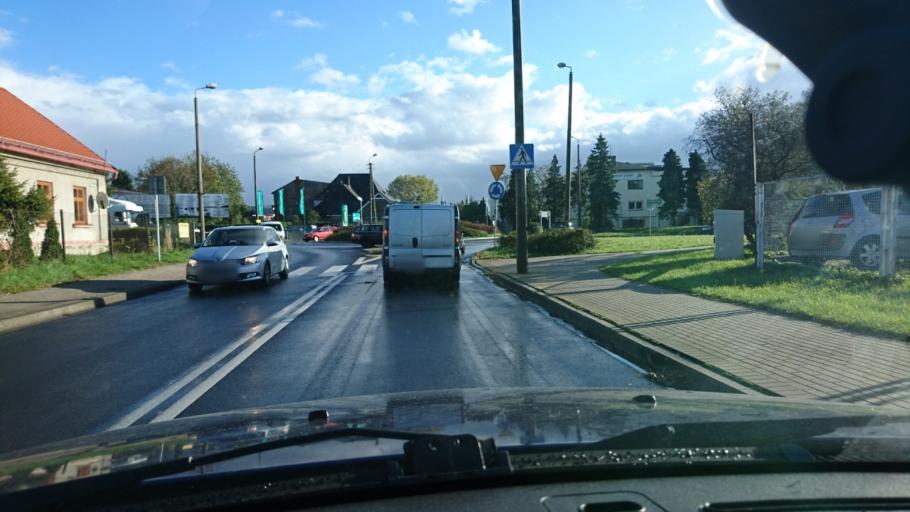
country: PL
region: Silesian Voivodeship
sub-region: Bielsko-Biala
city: Bielsko-Biala
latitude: 49.8413
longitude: 19.0515
